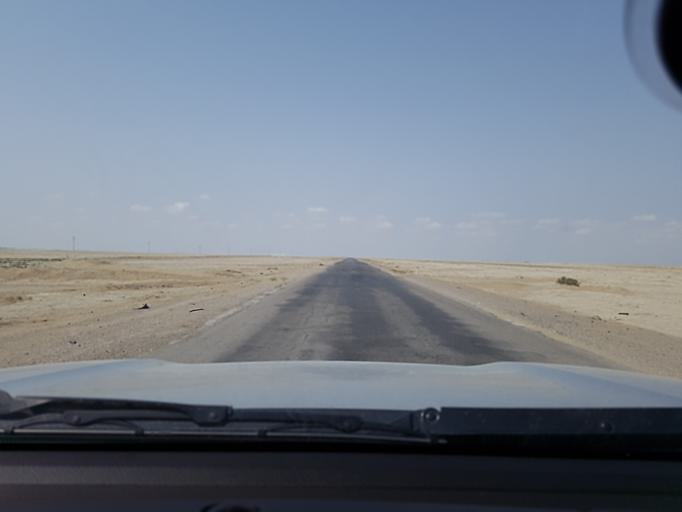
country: TM
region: Balkan
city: Gumdag
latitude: 38.6670
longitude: 54.4018
